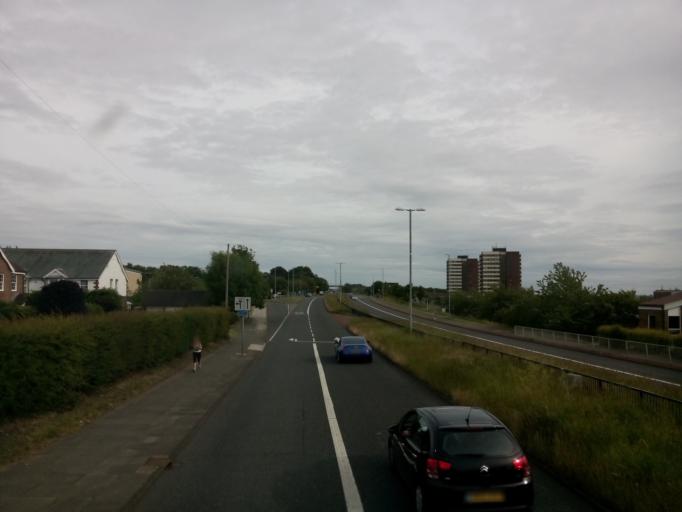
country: GB
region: England
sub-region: Gateshead
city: Lamesley
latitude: 54.9241
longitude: -1.5935
